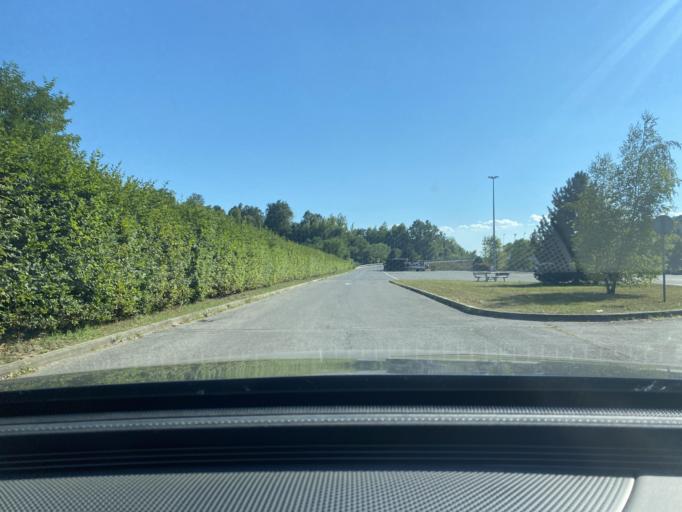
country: HR
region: Karlovacka
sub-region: Grad Karlovac
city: Karlovac
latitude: 45.4549
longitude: 15.3778
